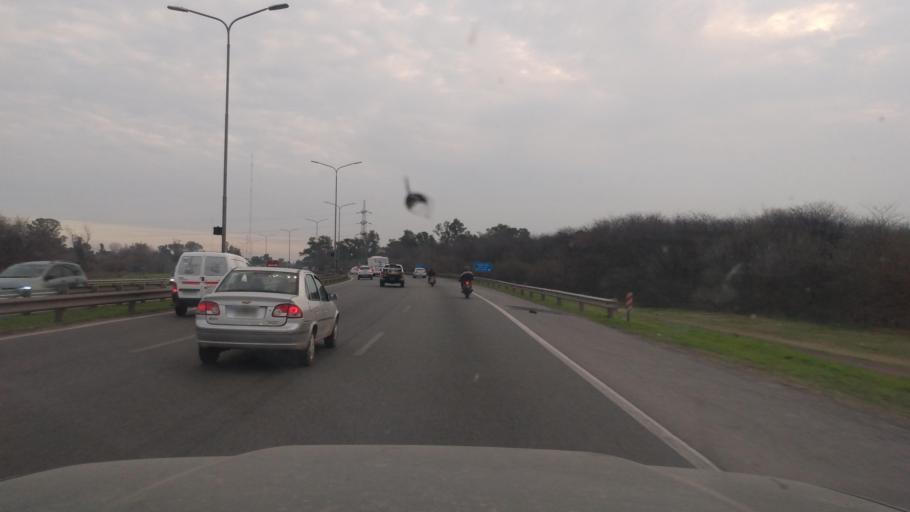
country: AR
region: Buenos Aires
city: Hurlingham
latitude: -34.5943
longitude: -58.6913
